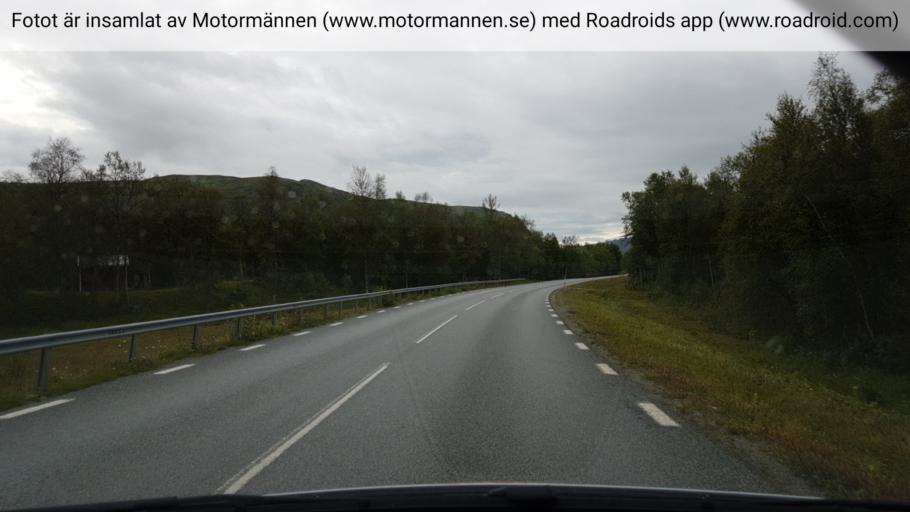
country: NO
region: Nordland
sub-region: Rana
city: Mo i Rana
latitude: 65.9347
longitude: 15.0275
